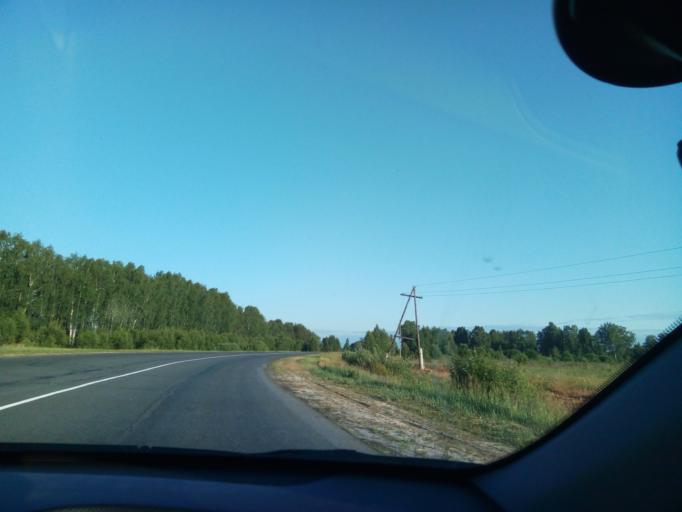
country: RU
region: Nizjnij Novgorod
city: Voznesenskoye
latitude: 54.8553
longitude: 42.8867
